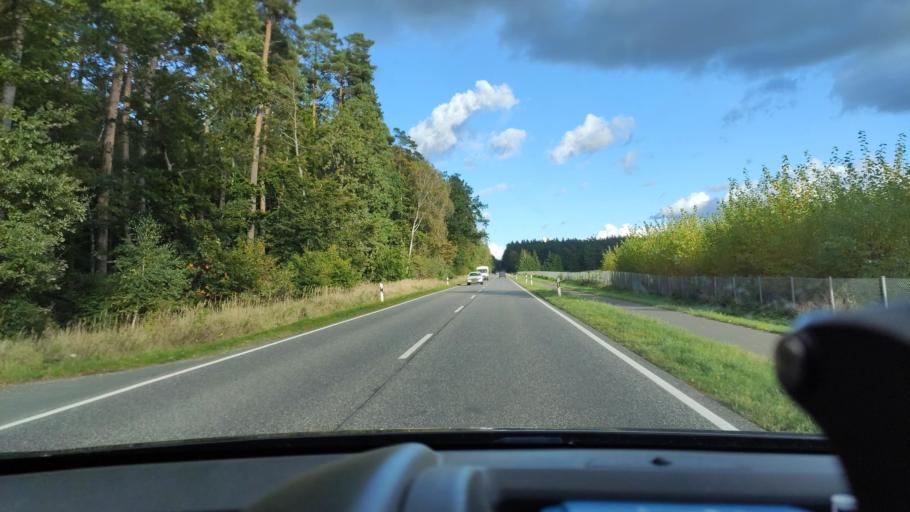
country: DE
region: Mecklenburg-Vorpommern
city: Muhl Rosin
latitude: 53.7719
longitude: 12.2989
